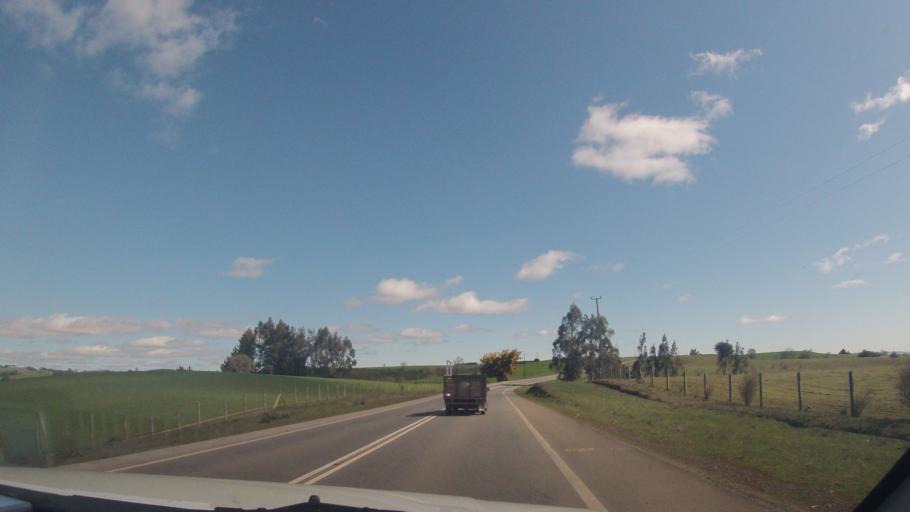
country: CL
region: Araucania
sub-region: Provincia de Malleco
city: Traiguen
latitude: -38.2002
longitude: -72.7697
